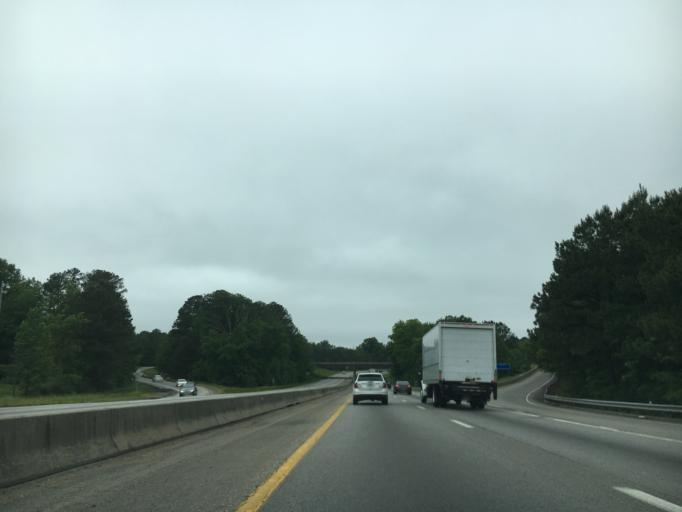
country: US
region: Virginia
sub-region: City of Petersburg
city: Petersburg
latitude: 37.1992
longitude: -77.4232
